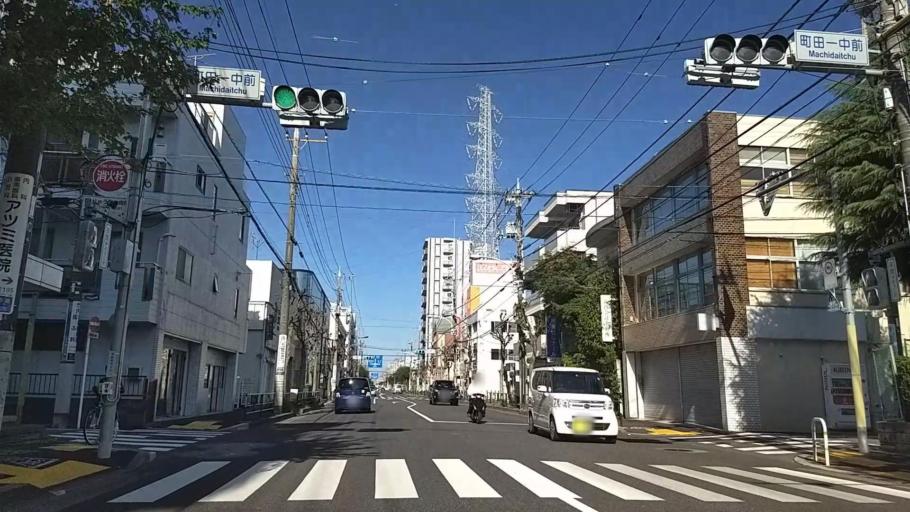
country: JP
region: Tokyo
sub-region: Machida-shi
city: Machida
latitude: 35.5508
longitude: 139.4454
